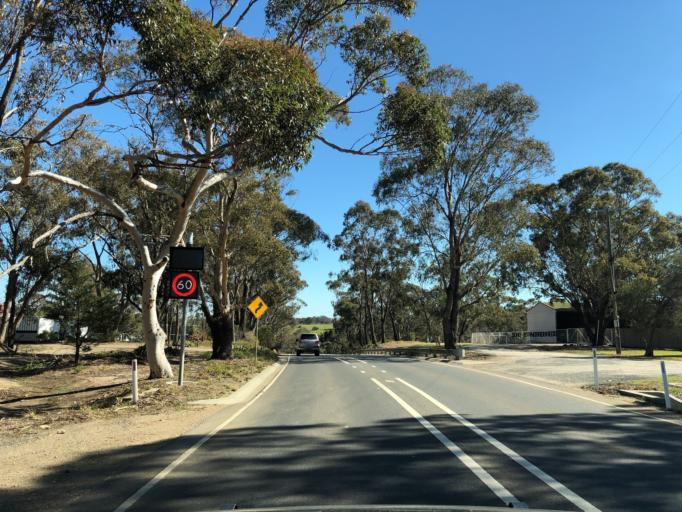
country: AU
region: Victoria
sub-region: Melton
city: Melton West
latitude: -37.6166
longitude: 144.5304
